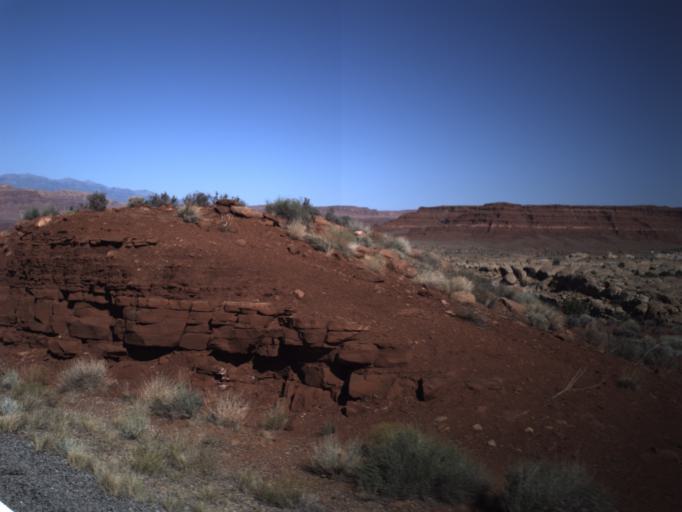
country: US
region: Utah
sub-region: San Juan County
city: Blanding
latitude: 37.8098
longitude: -110.3307
